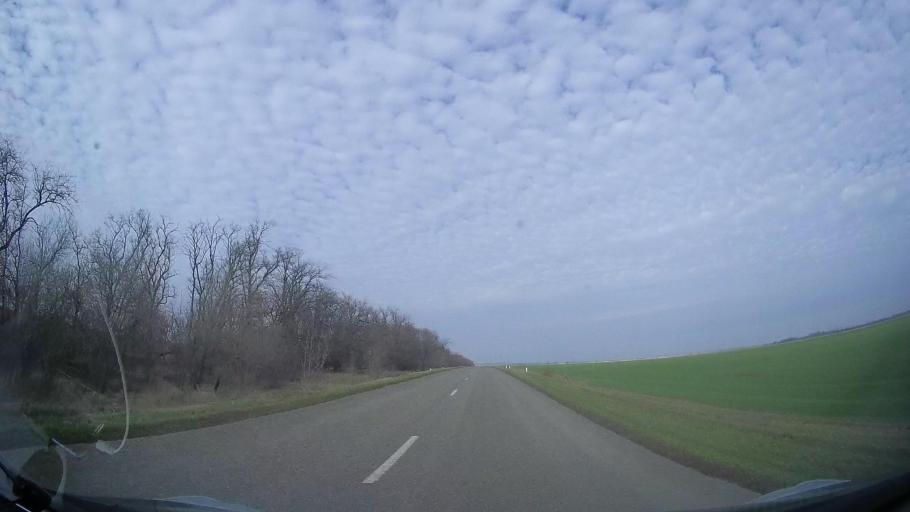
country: RU
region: Rostov
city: Gigant
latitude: 46.9337
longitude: 41.2433
